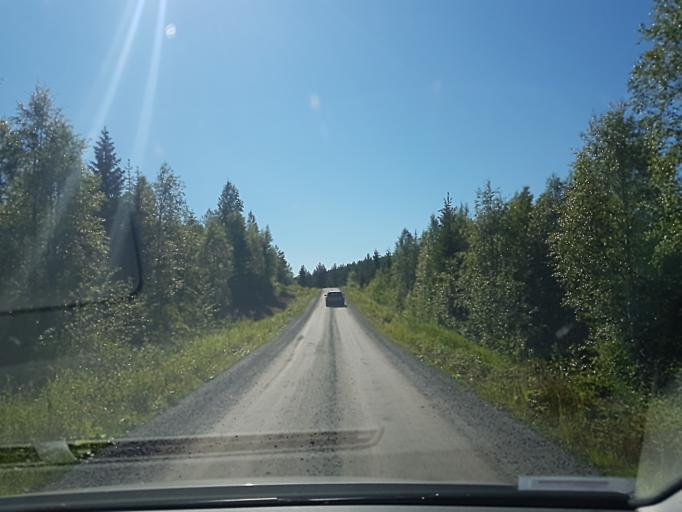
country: SE
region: Vaesternorrland
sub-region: OErnskoeldsviks Kommun
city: Bjasta
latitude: 63.1188
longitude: 18.3989
